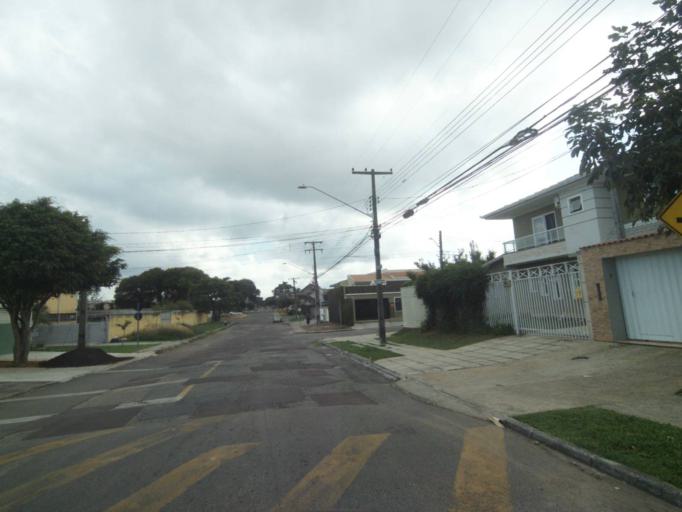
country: BR
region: Parana
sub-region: Pinhais
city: Pinhais
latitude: -25.4548
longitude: -49.2104
